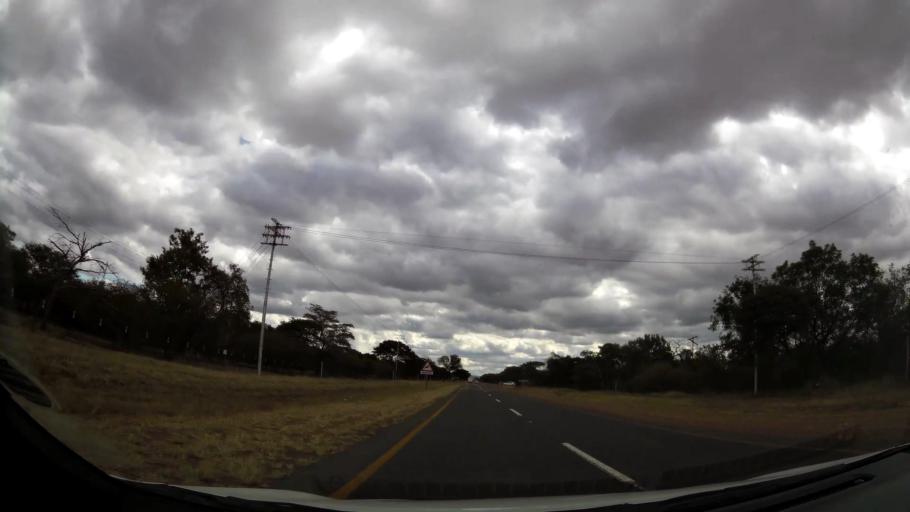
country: ZA
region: Limpopo
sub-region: Waterberg District Municipality
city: Modimolle
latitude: -24.7712
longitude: 28.4687
